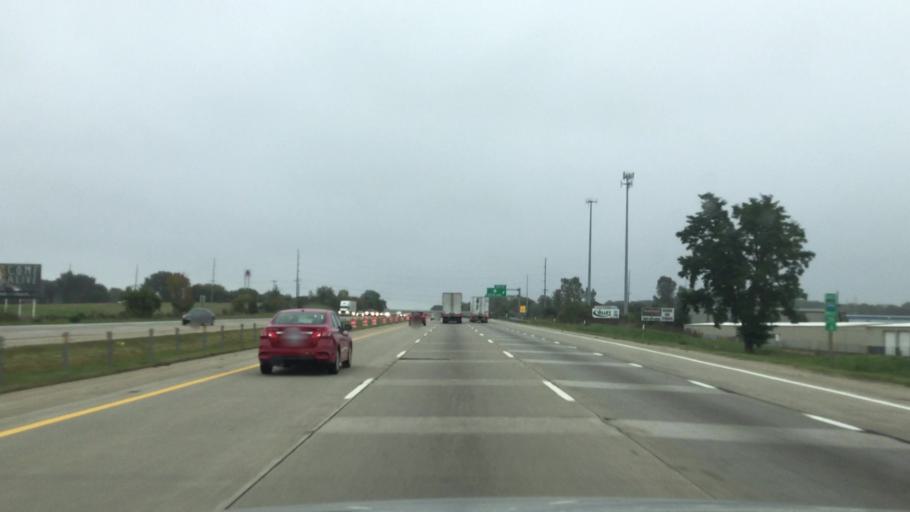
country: US
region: Michigan
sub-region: Berrien County
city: Fair Plain
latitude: 42.0570
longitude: -86.4652
